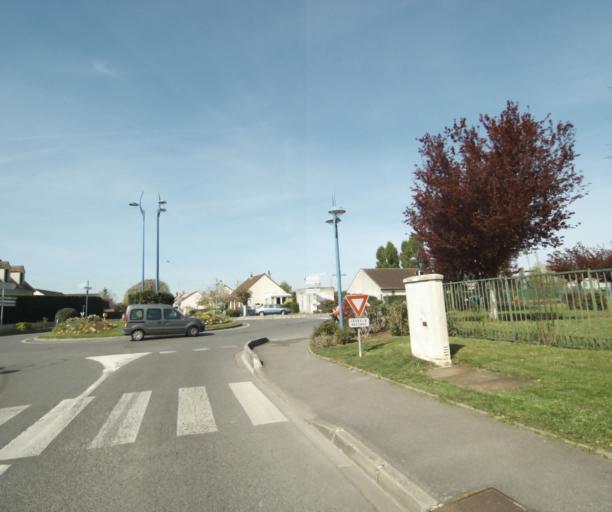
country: FR
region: Ile-de-France
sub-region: Departement de Seine-et-Marne
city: Nangis
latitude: 48.5505
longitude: 3.0162
